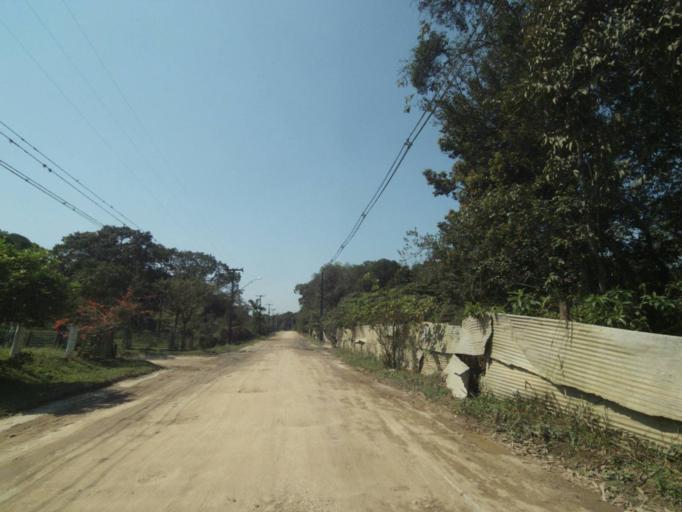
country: BR
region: Parana
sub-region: Paranagua
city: Paranagua
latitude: -25.5546
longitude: -48.5936
